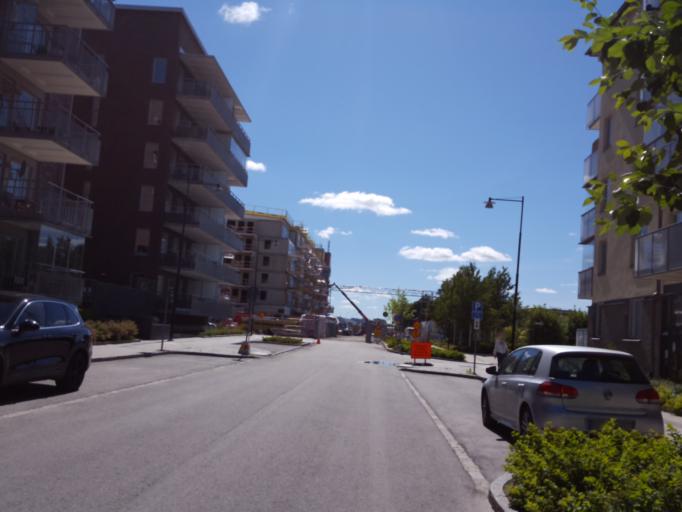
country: SE
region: Uppsala
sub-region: Uppsala Kommun
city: Uppsala
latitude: 59.8498
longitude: 17.6552
